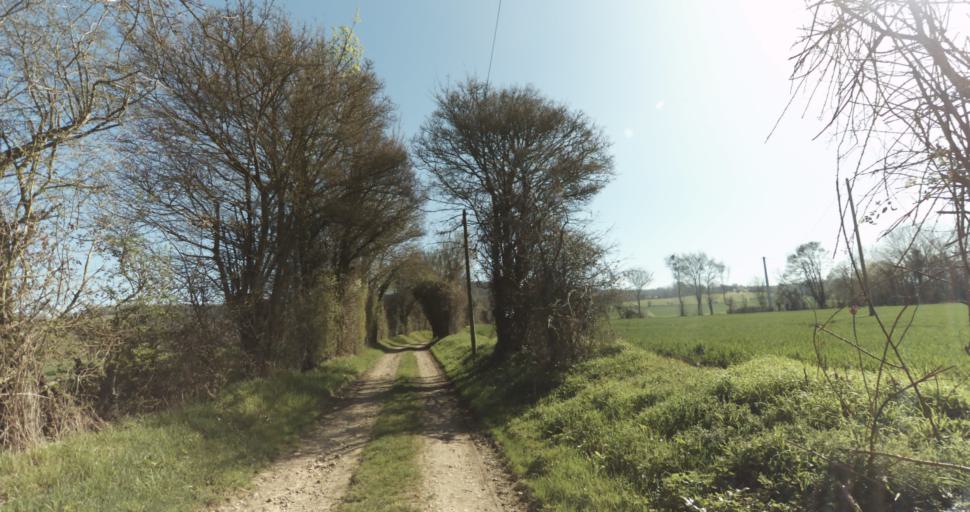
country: FR
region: Lower Normandy
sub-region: Departement du Calvados
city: Saint-Pierre-sur-Dives
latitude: 48.9734
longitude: 0.0538
